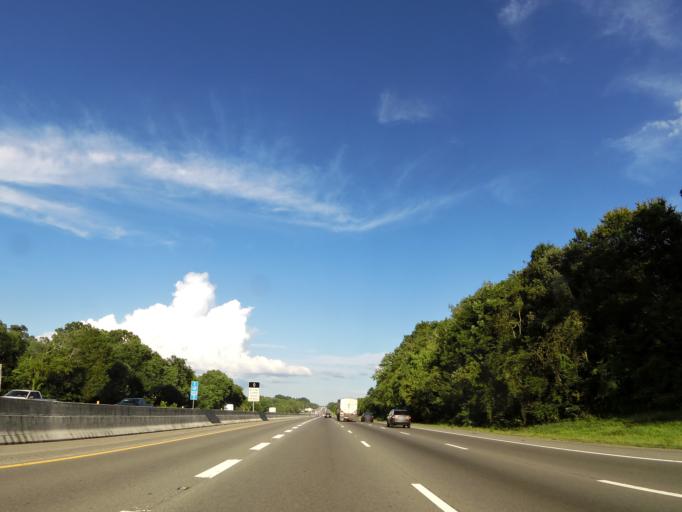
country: US
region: Tennessee
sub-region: Wilson County
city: Green Hill
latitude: 36.1692
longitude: -86.5774
